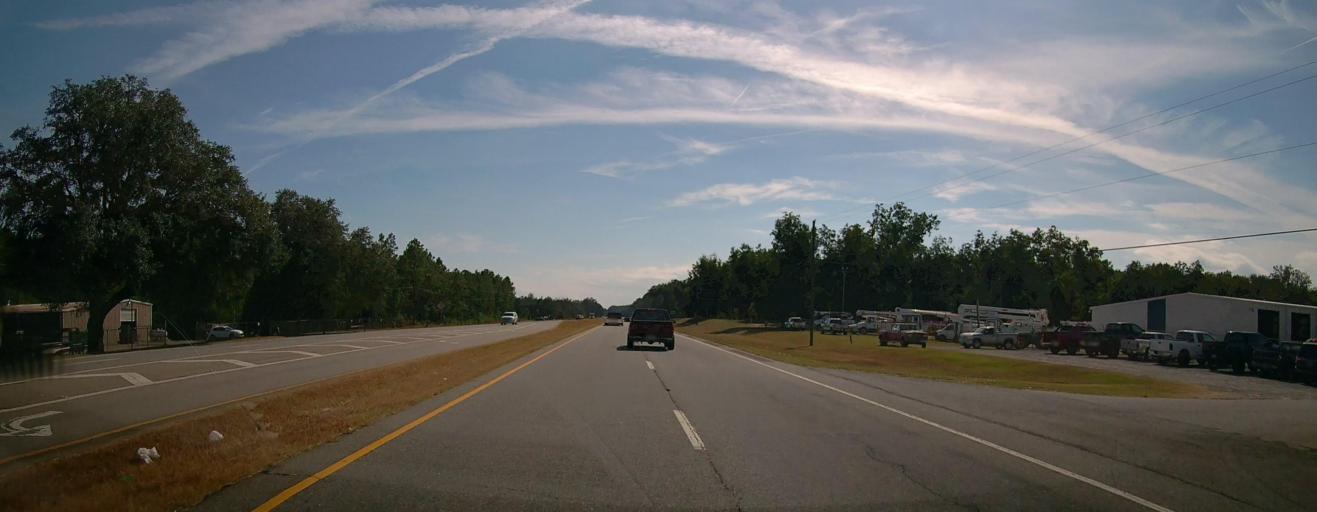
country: US
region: Georgia
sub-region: Dougherty County
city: Putney
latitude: 31.4830
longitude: -84.1168
